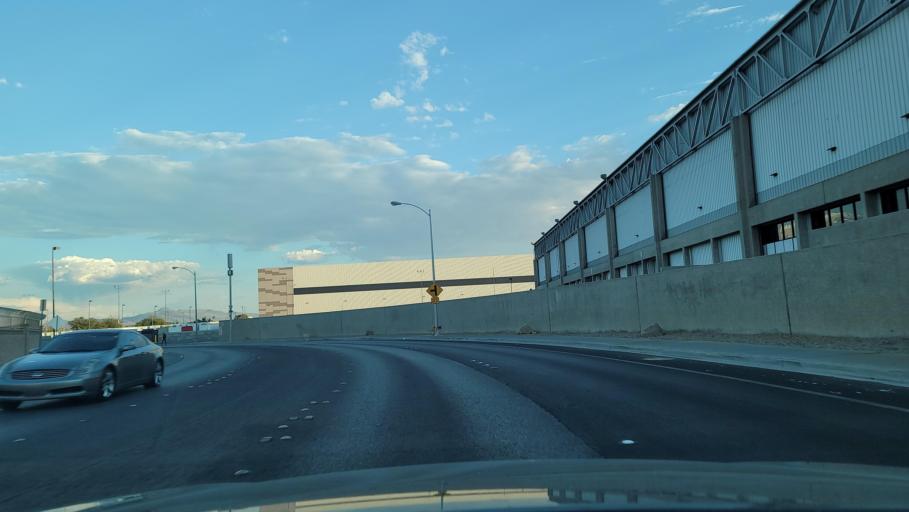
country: US
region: Nevada
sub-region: Clark County
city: Winchester
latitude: 36.1318
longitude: -115.1478
